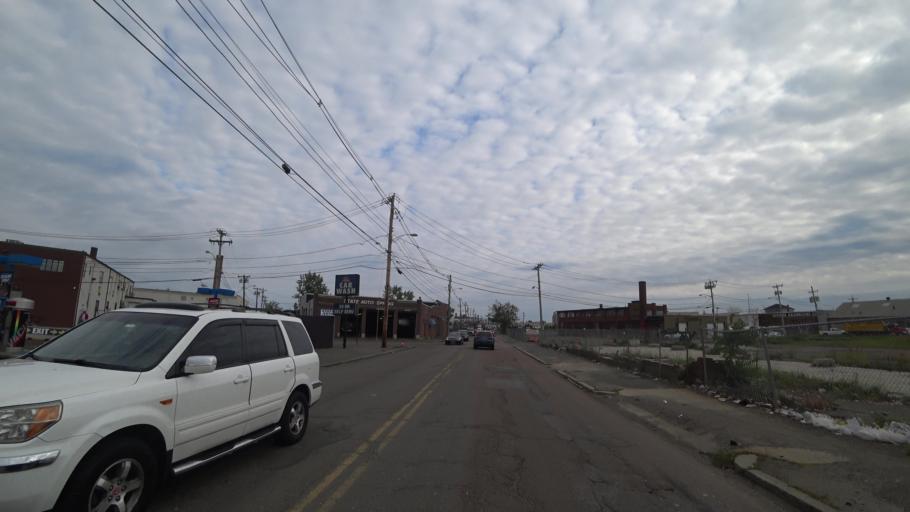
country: US
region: Massachusetts
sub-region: Middlesex County
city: Everett
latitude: 42.4022
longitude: -71.0526
